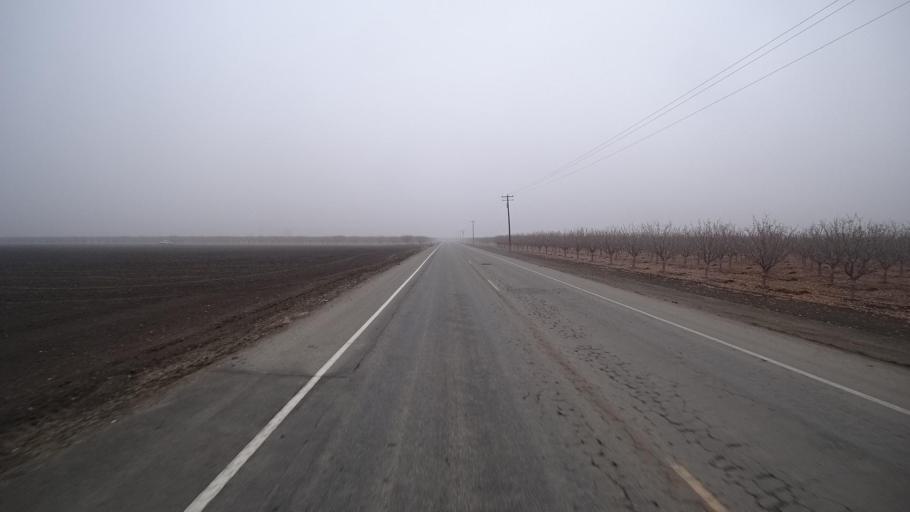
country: US
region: California
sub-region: Kern County
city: Buttonwillow
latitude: 35.4044
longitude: -119.5184
